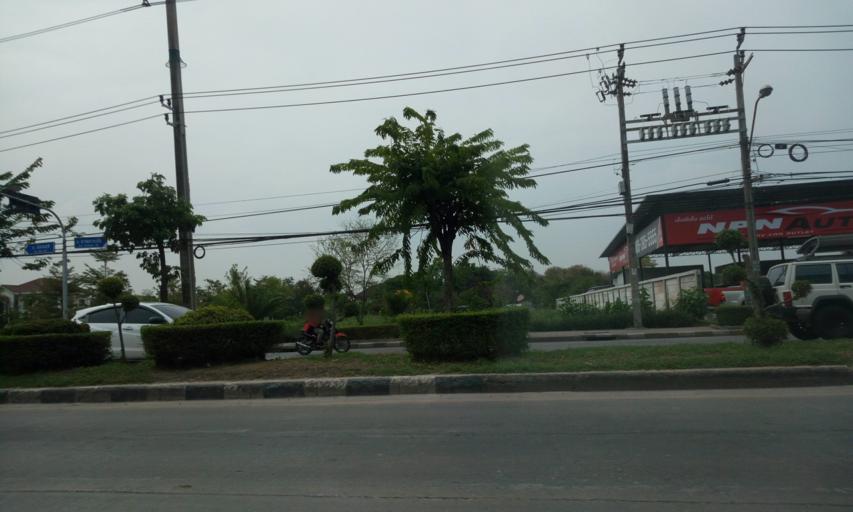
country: TH
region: Bangkok
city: Saphan Sung
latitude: 13.7219
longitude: 100.7072
